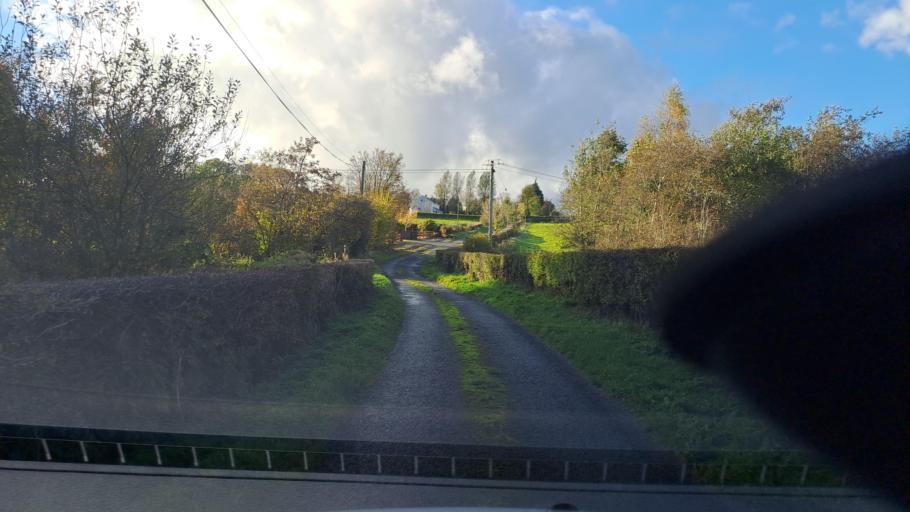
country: IE
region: Ulster
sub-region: An Cabhan
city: Bailieborough
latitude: 53.9331
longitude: -6.9437
